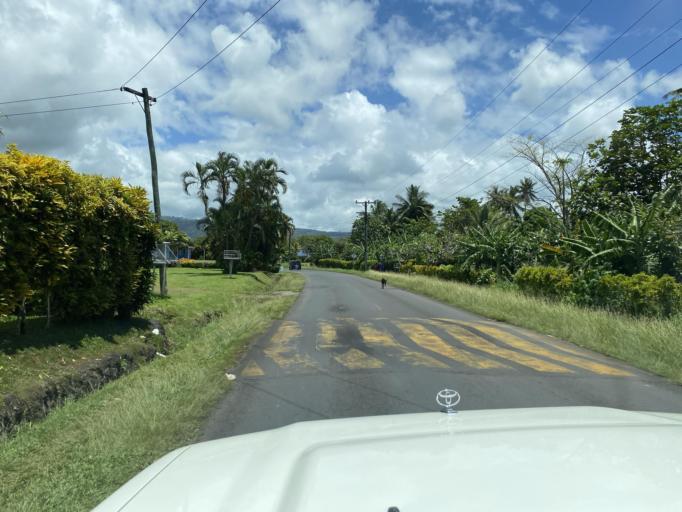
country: WS
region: Tuamasaga
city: Apia
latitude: -13.8435
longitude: -171.7757
